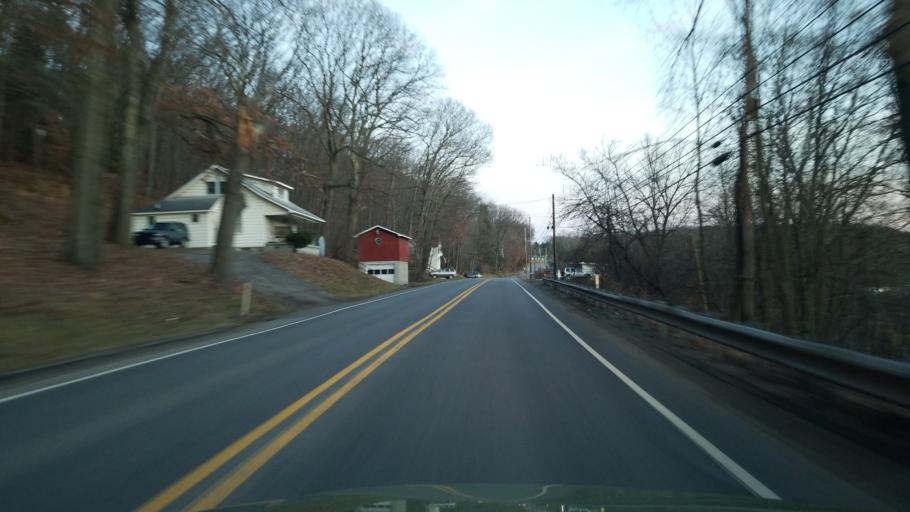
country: US
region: Pennsylvania
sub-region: Jefferson County
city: Albion
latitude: 40.9528
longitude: -78.9464
